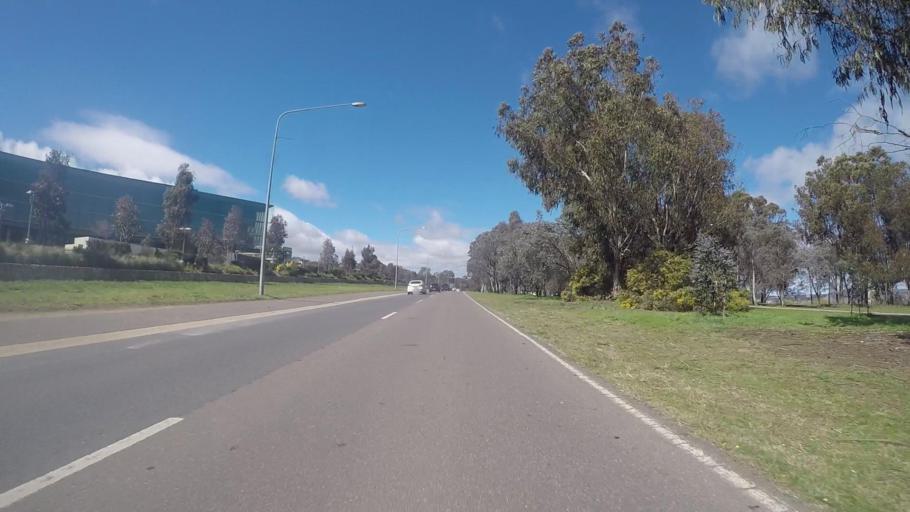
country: AU
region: Australian Capital Territory
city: Canberra
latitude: -35.2930
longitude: 149.1434
